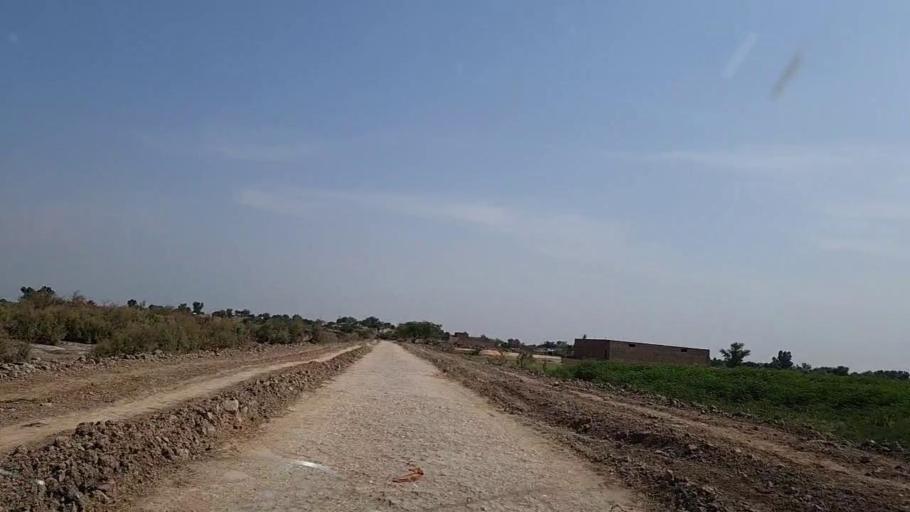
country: PK
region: Sindh
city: Khanpur
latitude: 27.7535
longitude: 69.3370
